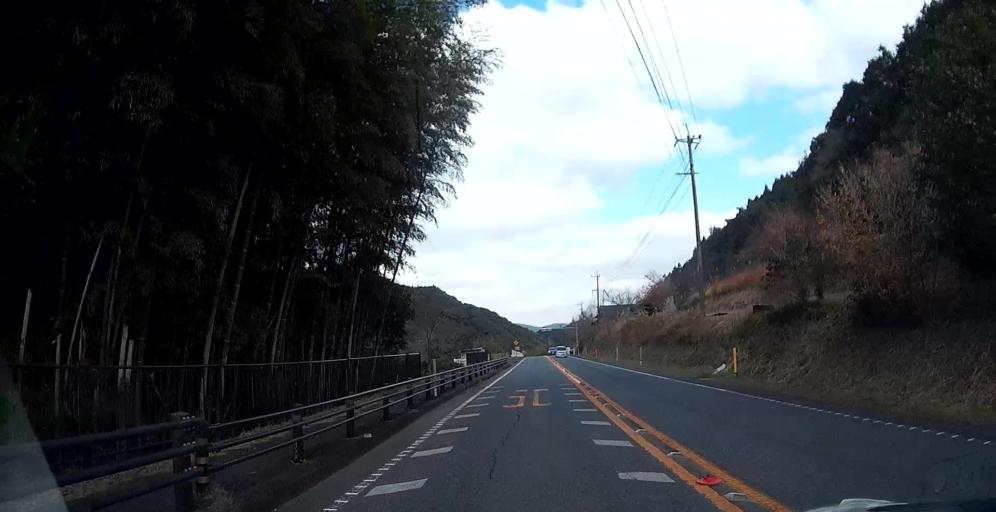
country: JP
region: Kumamoto
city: Yatsushiro
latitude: 32.3787
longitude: 130.5362
